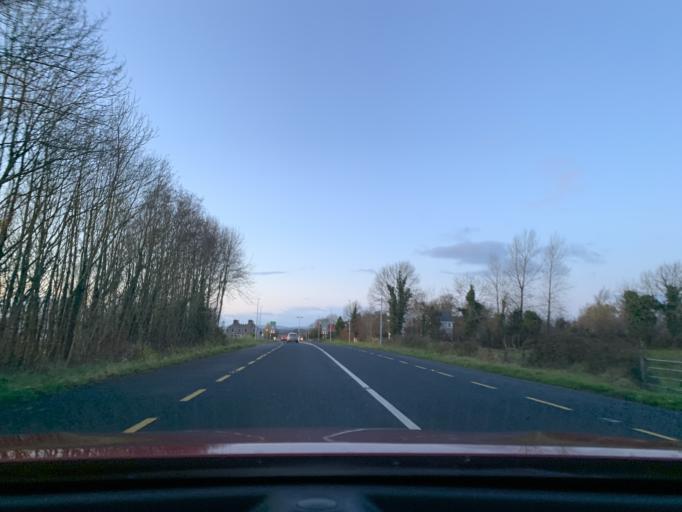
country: IE
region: Connaught
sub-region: County Leitrim
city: Carrick-on-Shannon
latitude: 53.8991
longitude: -7.9541
